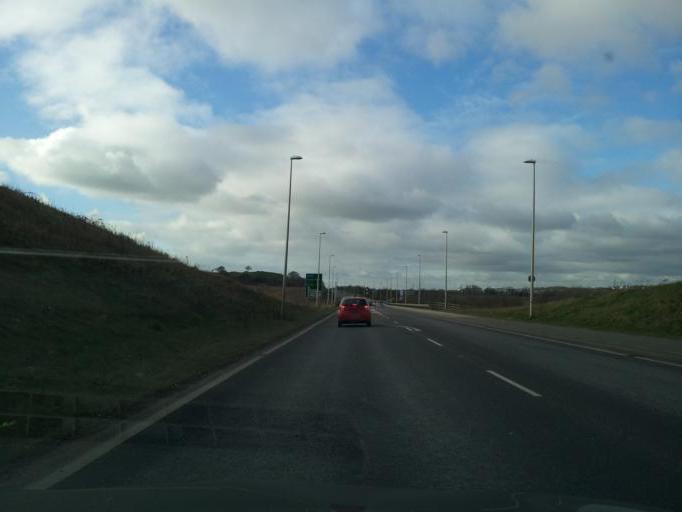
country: GB
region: England
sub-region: Nottinghamshire
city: Mansfield
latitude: 53.1232
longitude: -1.2126
